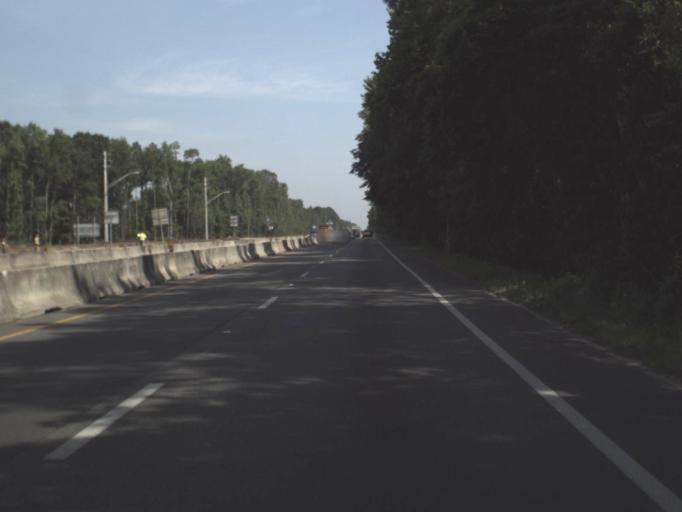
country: US
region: Florida
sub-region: Saint Johns County
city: Palm Valley
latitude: 30.1330
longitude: -81.5078
